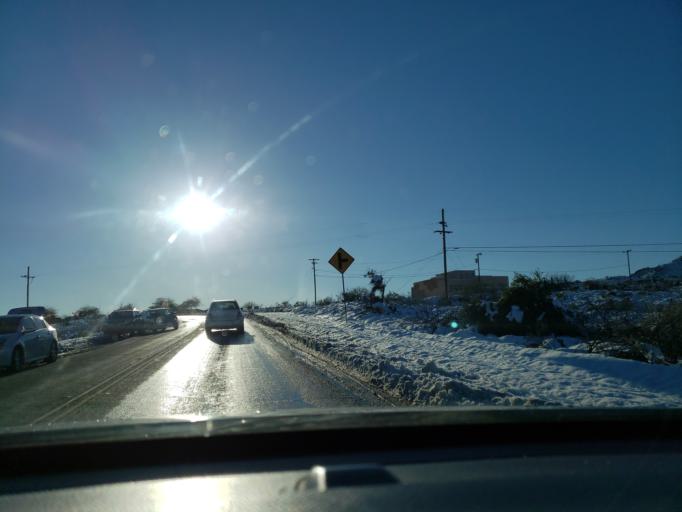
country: US
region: Arizona
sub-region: Maricopa County
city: Carefree
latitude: 33.8670
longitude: -111.8269
